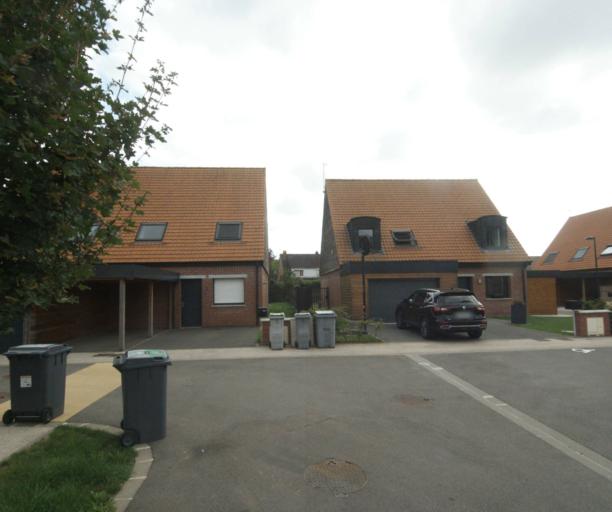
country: FR
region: Nord-Pas-de-Calais
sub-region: Departement du Nord
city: Chereng
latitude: 50.6107
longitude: 3.2006
